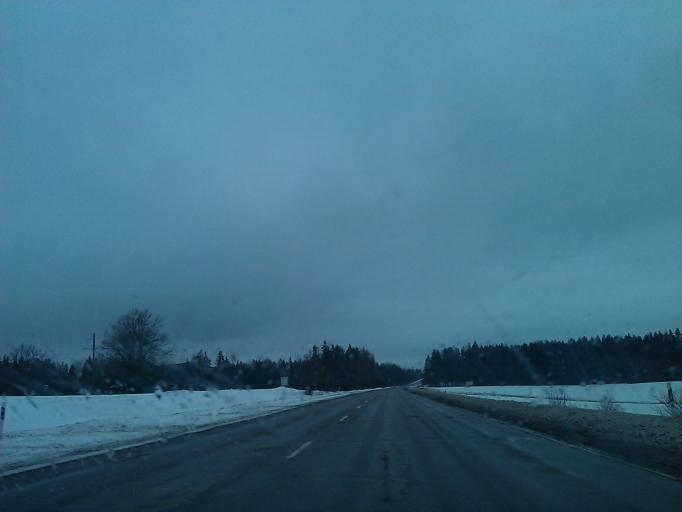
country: LV
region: Amatas Novads
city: Drabesi
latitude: 57.2735
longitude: 25.2799
